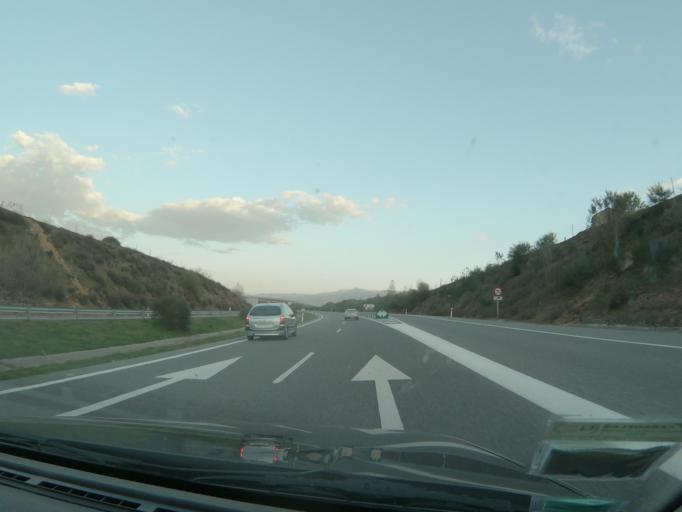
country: ES
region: Castille and Leon
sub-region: Provincia de Leon
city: Villafranca del Bierzo
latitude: 42.5863
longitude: -6.7913
